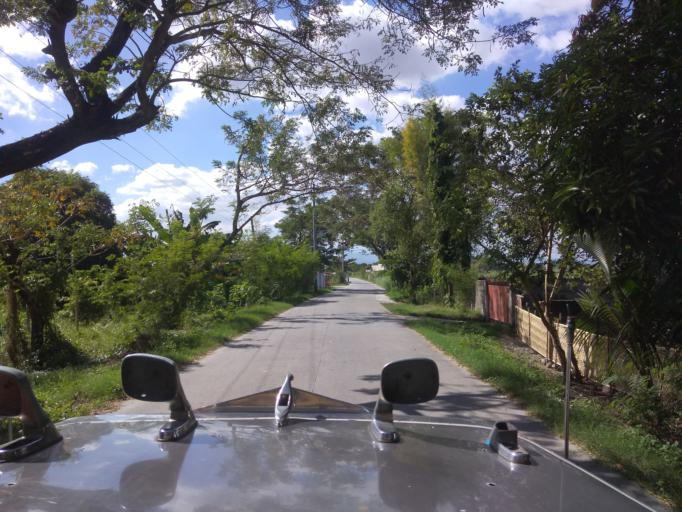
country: PH
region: Central Luzon
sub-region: Province of Pampanga
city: Santa Rita
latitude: 15.0302
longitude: 120.6284
